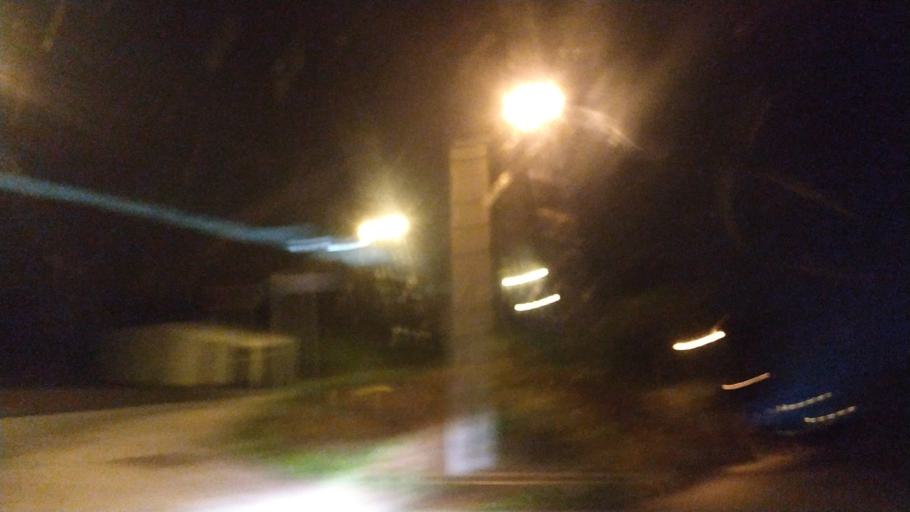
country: ES
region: Galicia
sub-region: Provincia de Lugo
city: Lugo
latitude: 42.9970
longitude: -7.5675
